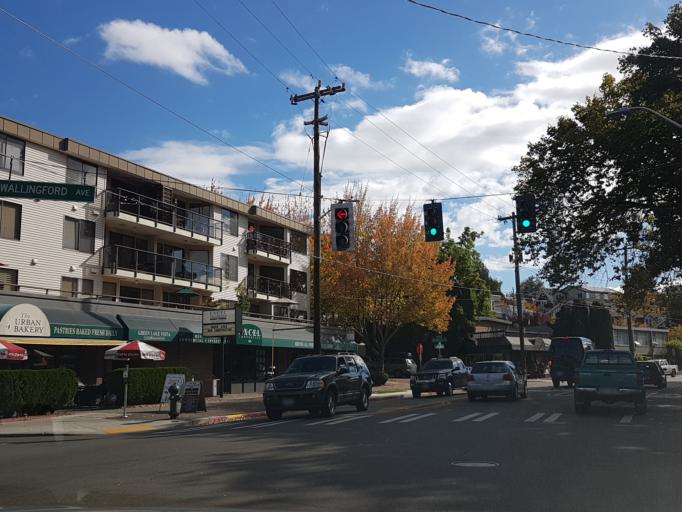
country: US
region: Washington
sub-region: King County
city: Shoreline
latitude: 47.6856
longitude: -122.3369
